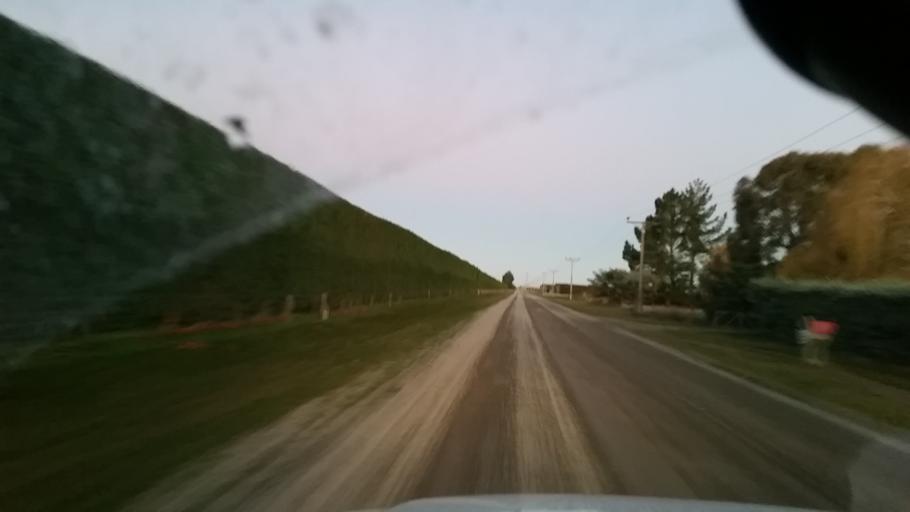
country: NZ
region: Canterbury
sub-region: Ashburton District
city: Tinwald
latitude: -43.9709
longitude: 171.6370
